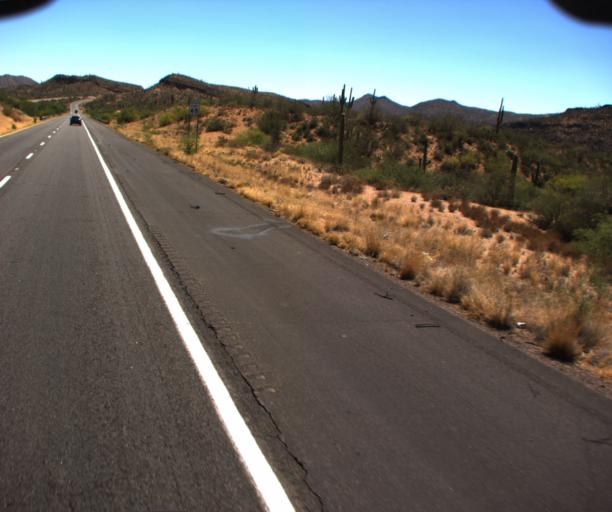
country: US
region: Arizona
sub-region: Maricopa County
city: Rio Verde
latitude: 33.7624
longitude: -111.4956
